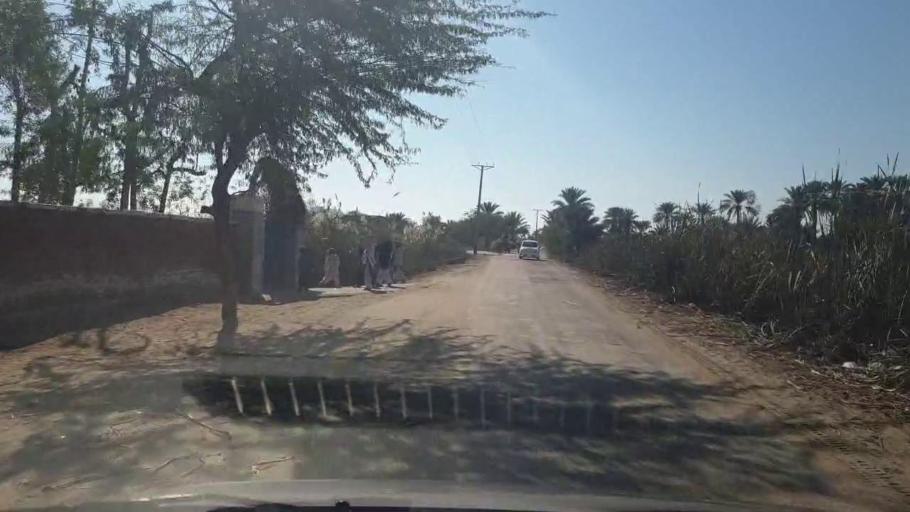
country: PK
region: Sindh
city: Bozdar
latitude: 27.2446
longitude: 68.6522
